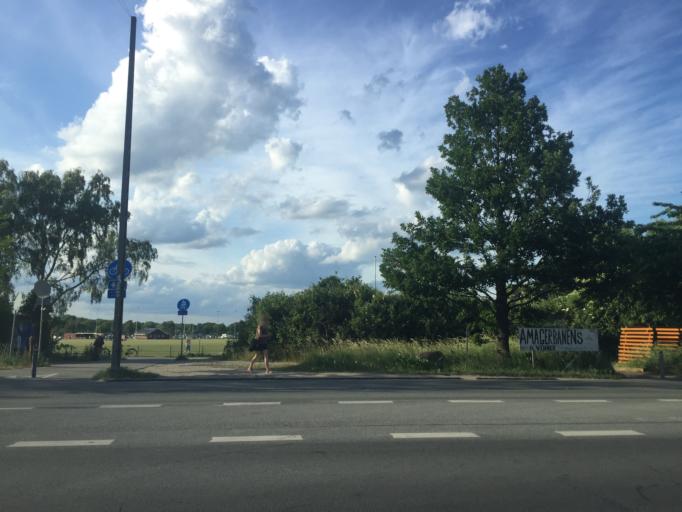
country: DK
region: Capital Region
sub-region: Kobenhavn
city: Christianshavn
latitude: 55.6694
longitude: 12.6113
